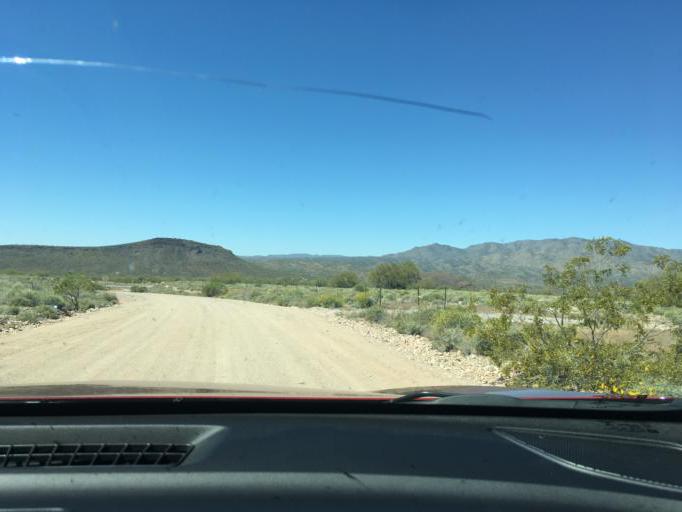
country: US
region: Arizona
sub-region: Yavapai County
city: Bagdad
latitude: 34.6111
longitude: -113.5214
